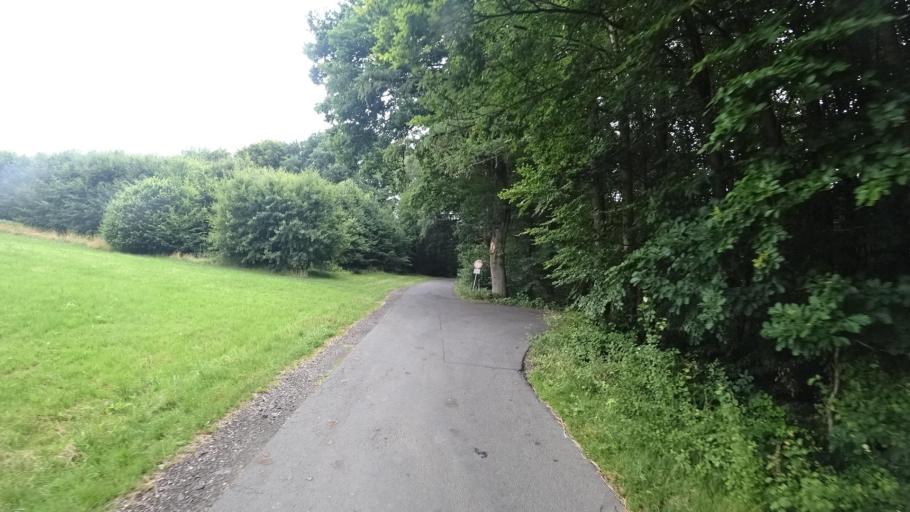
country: DE
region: Rheinland-Pfalz
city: Seifen
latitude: 50.6744
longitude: 7.5115
